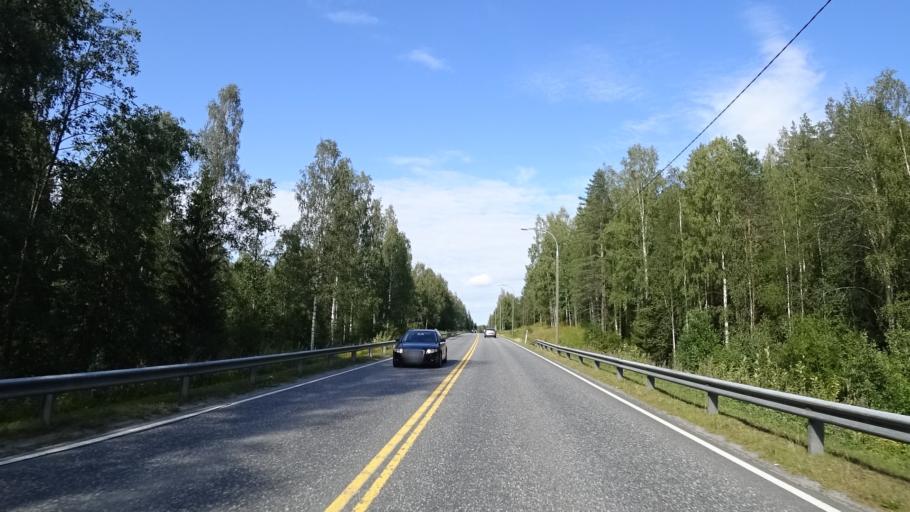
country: FI
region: North Karelia
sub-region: Joensuu
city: Eno
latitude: 62.7856
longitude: 30.0789
